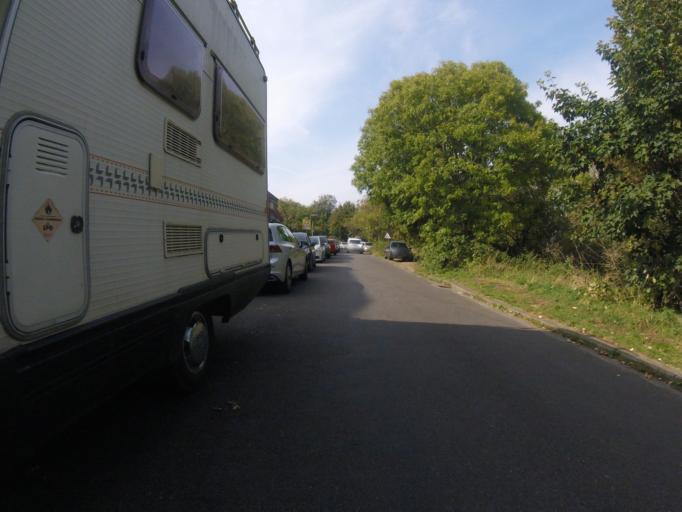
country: GB
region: England
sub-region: East Sussex
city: Portslade
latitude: 50.8528
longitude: -0.1885
